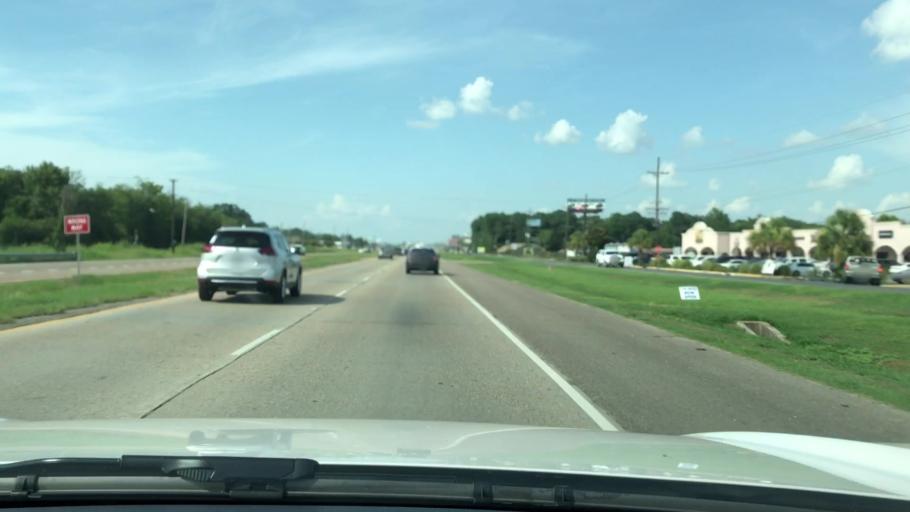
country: US
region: Louisiana
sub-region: West Baton Rouge Parish
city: Brusly
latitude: 30.4086
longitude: -91.2286
